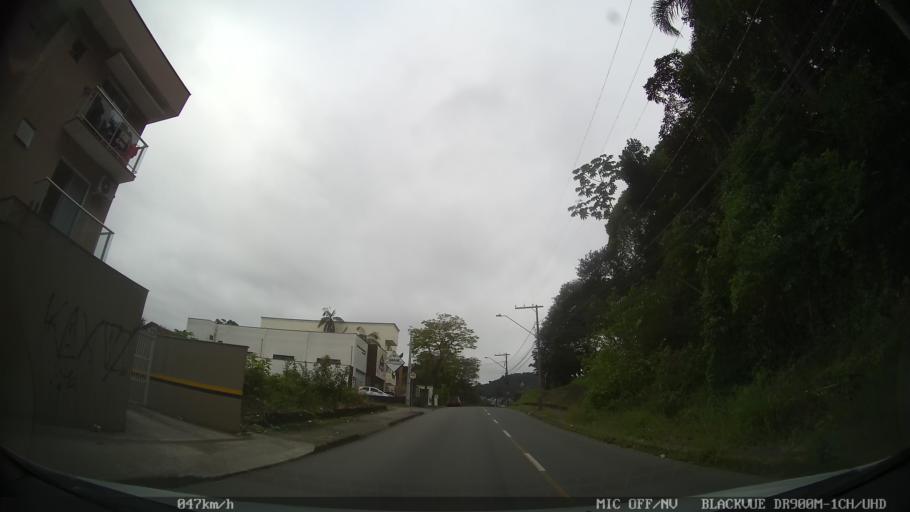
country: BR
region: Santa Catarina
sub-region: Joinville
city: Joinville
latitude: -26.2628
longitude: -48.8466
